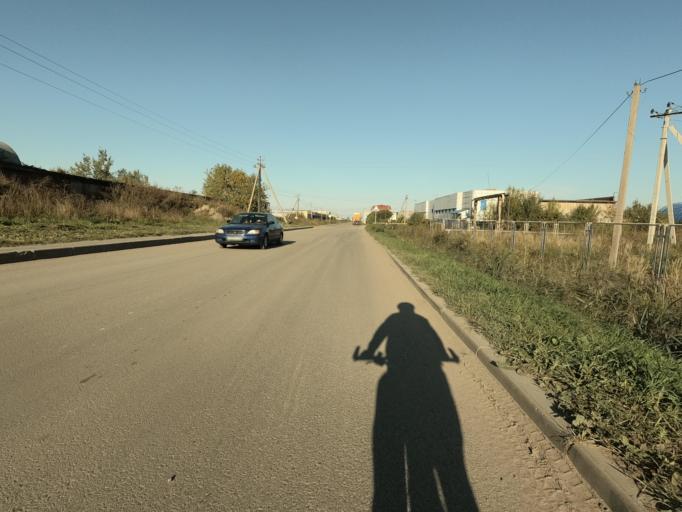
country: RU
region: St.-Petersburg
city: Petro-Slavyanka
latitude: 59.7620
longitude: 30.4805
